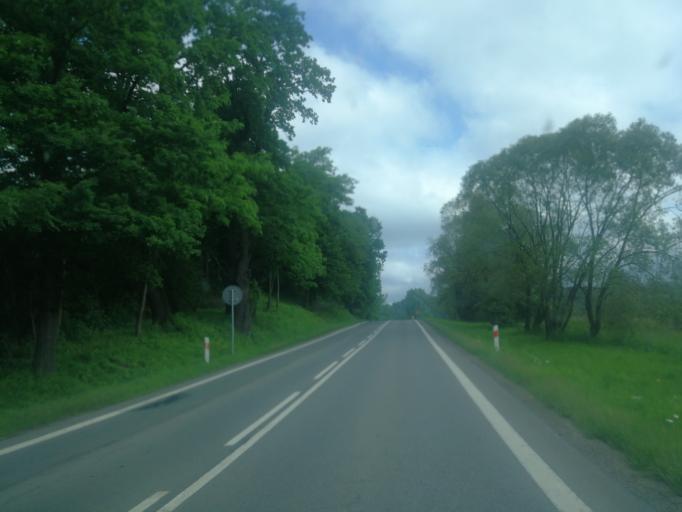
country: PL
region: Subcarpathian Voivodeship
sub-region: Powiat leski
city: Lesko
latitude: 49.4839
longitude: 22.3233
